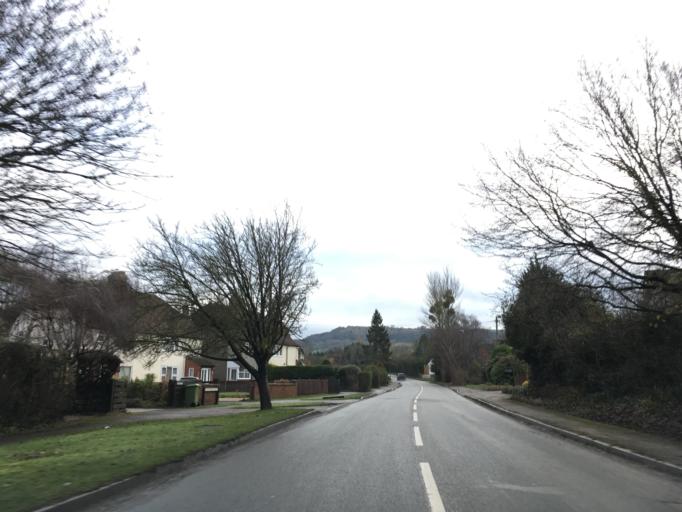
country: GB
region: England
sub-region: Gloucestershire
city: Shurdington
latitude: 51.8676
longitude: -2.1104
